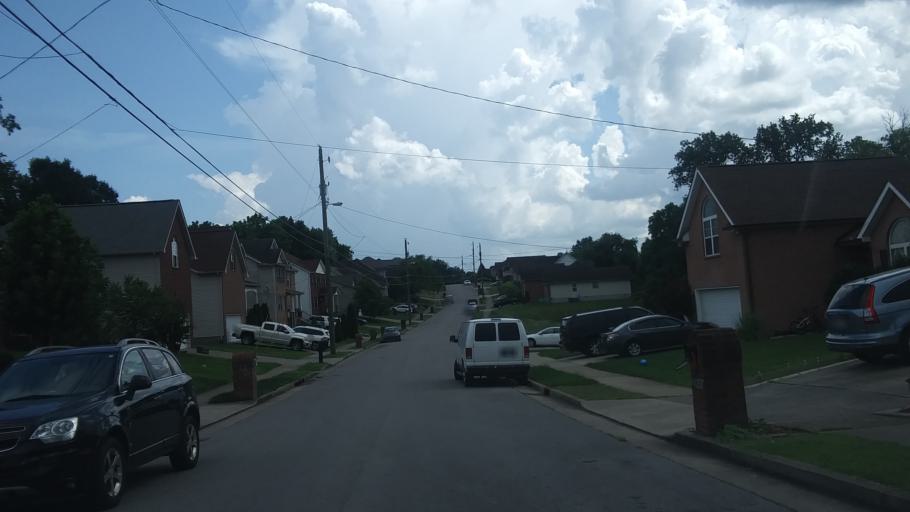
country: US
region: Tennessee
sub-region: Davidson County
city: Oak Hill
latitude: 36.0716
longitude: -86.7116
